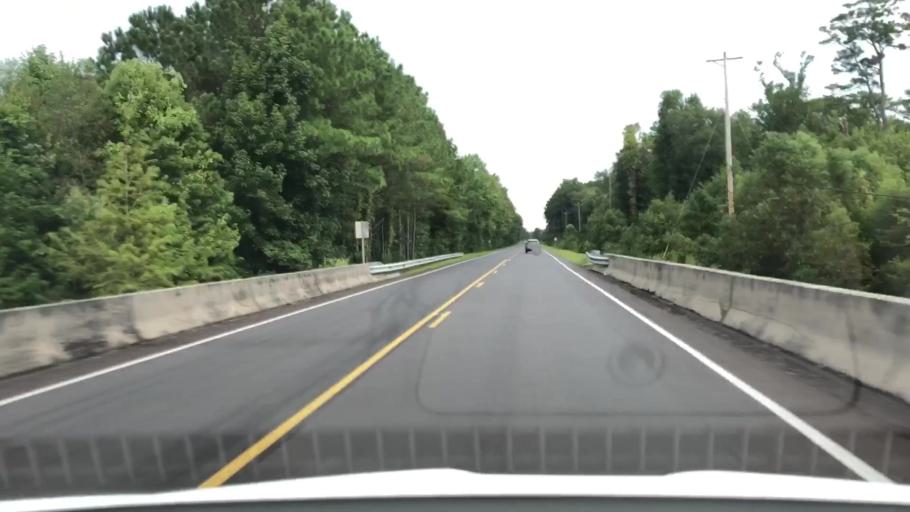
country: US
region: North Carolina
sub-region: Jones County
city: Maysville
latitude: 34.8716
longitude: -77.1964
